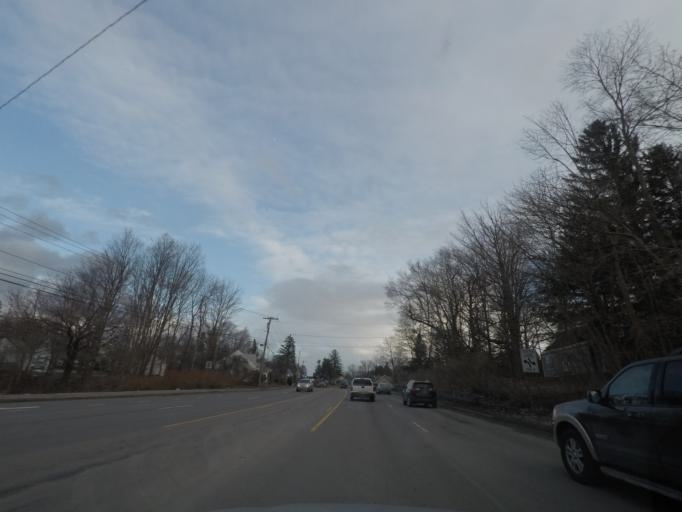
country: US
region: New York
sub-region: Oneida County
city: New Hartford
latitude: 43.0784
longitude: -75.3142
